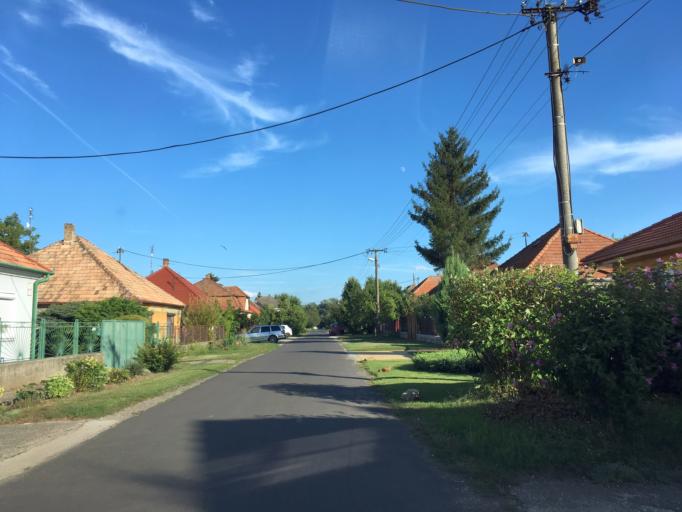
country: SK
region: Nitriansky
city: Svodin
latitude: 47.9003
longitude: 18.4117
